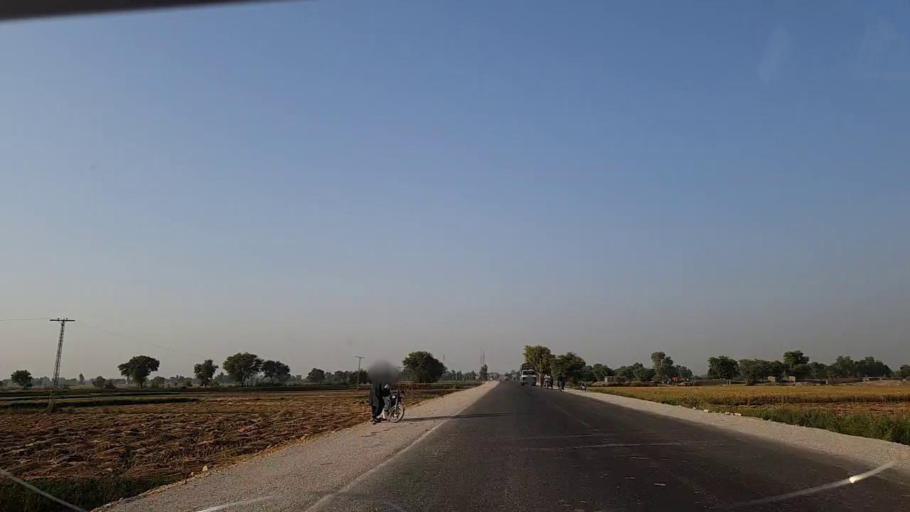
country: PK
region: Sindh
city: Rustam jo Goth
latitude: 27.9537
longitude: 68.8084
